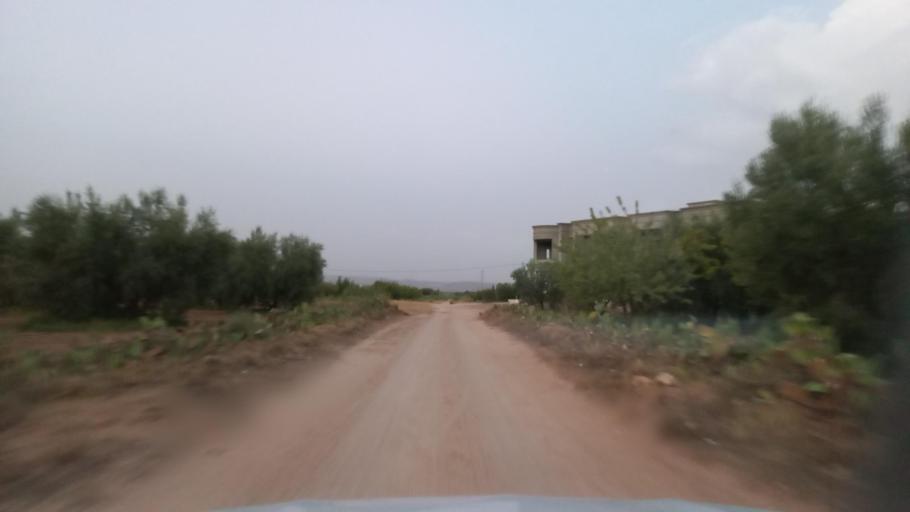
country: TN
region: Al Qasrayn
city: Kasserine
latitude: 35.2782
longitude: 9.0334
